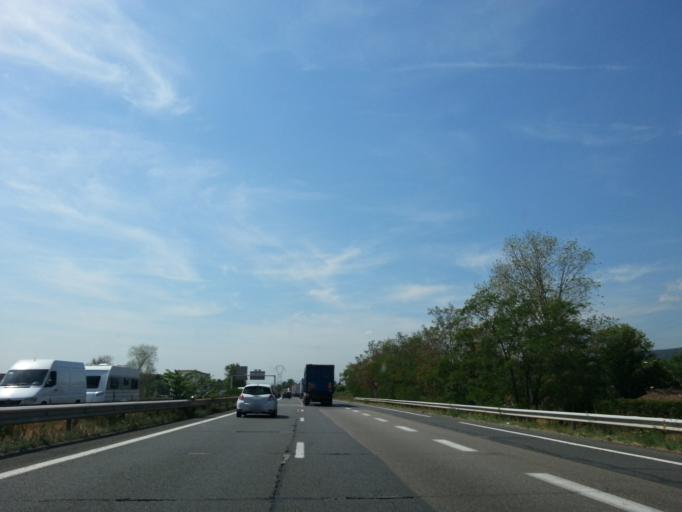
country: FR
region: Alsace
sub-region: Departement du Bas-Rhin
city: Chatenois
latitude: 48.2621
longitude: 7.4181
